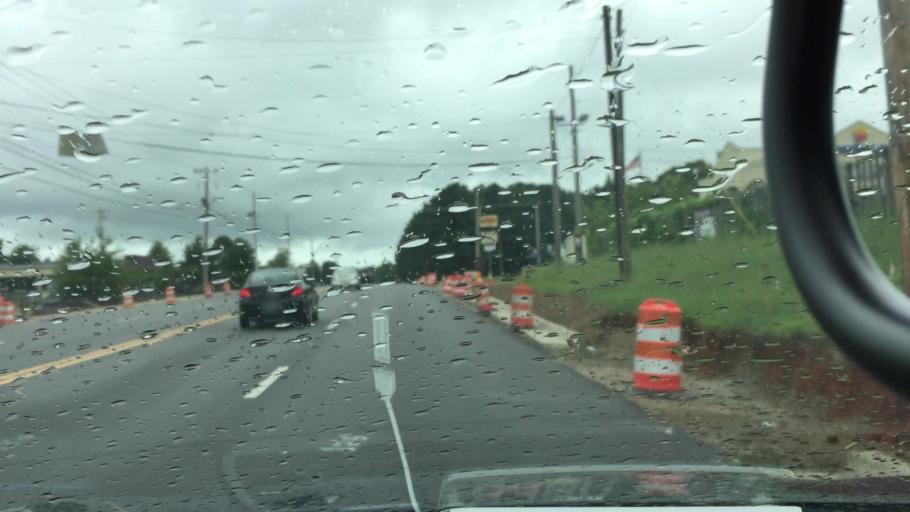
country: US
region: Alabama
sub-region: Lee County
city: Opelika
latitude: 32.6452
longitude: -85.3549
